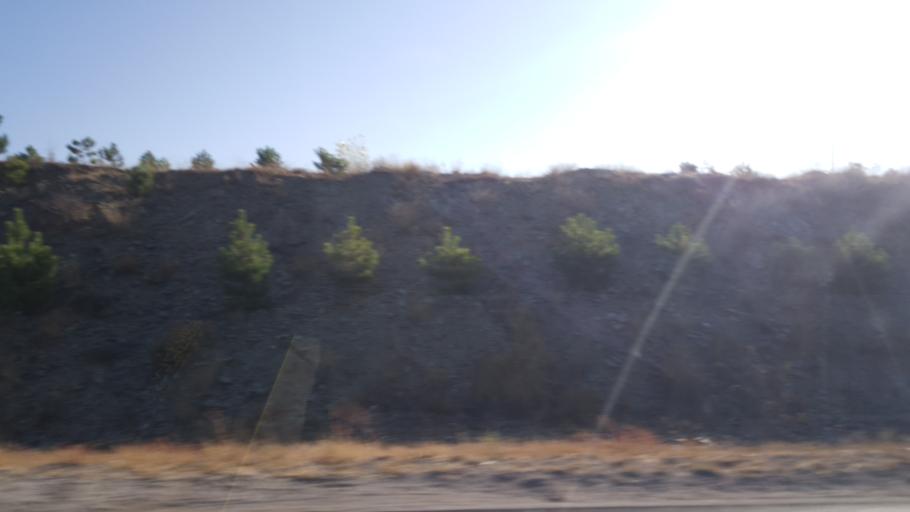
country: TR
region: Ankara
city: Cankaya
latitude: 39.8483
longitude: 32.8927
